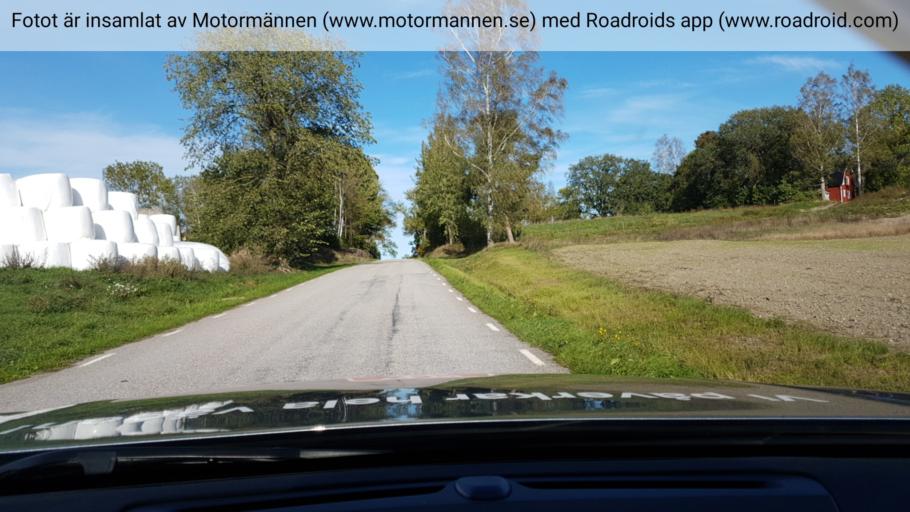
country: SE
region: OEstergoetland
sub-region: Valdemarsviks Kommun
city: Valdemarsvik
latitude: 58.1022
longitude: 16.6369
